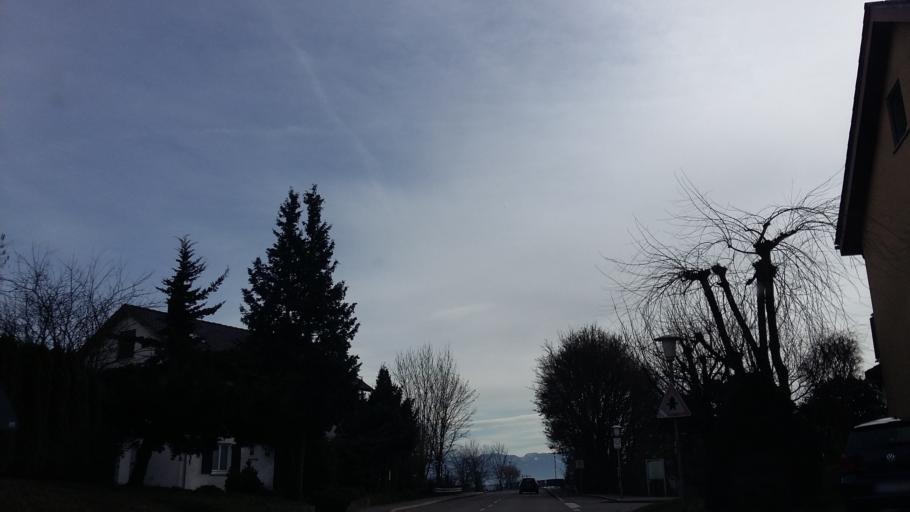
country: DE
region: Bavaria
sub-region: Swabia
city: Nonnenhorn
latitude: 47.5736
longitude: 9.6355
